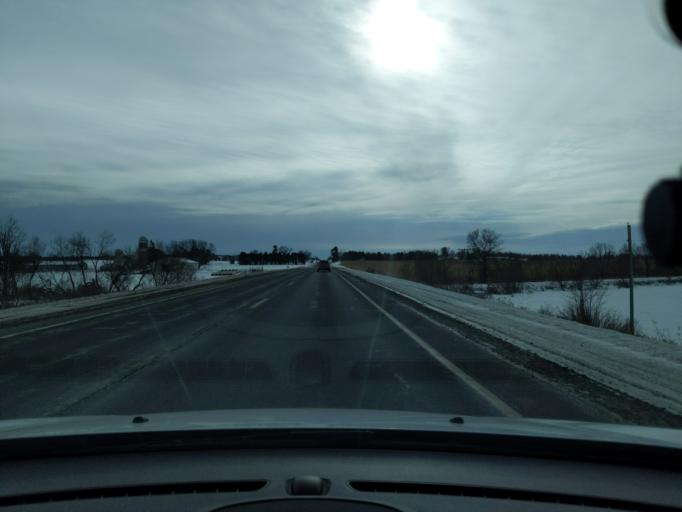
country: US
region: Wisconsin
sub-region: Barron County
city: Turtle Lake
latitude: 45.3865
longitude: -92.1667
